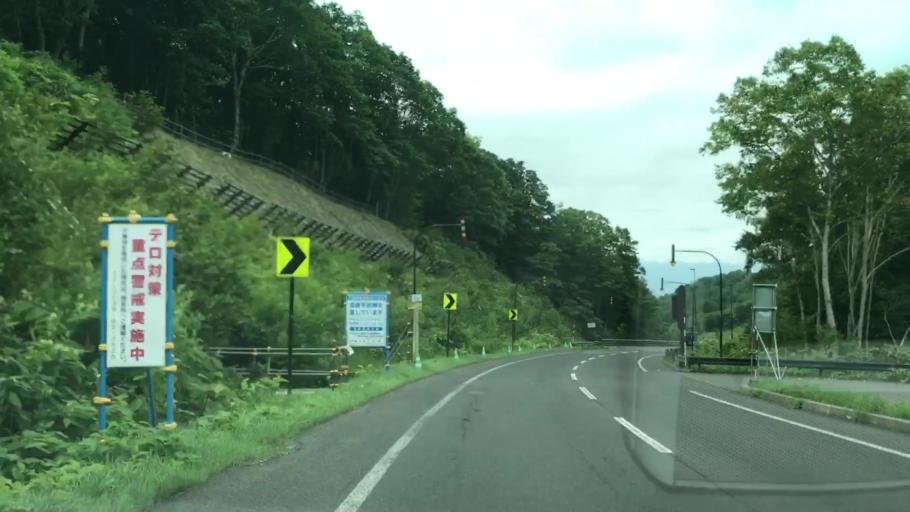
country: JP
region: Hokkaido
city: Otaru
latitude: 42.9616
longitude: 140.8784
